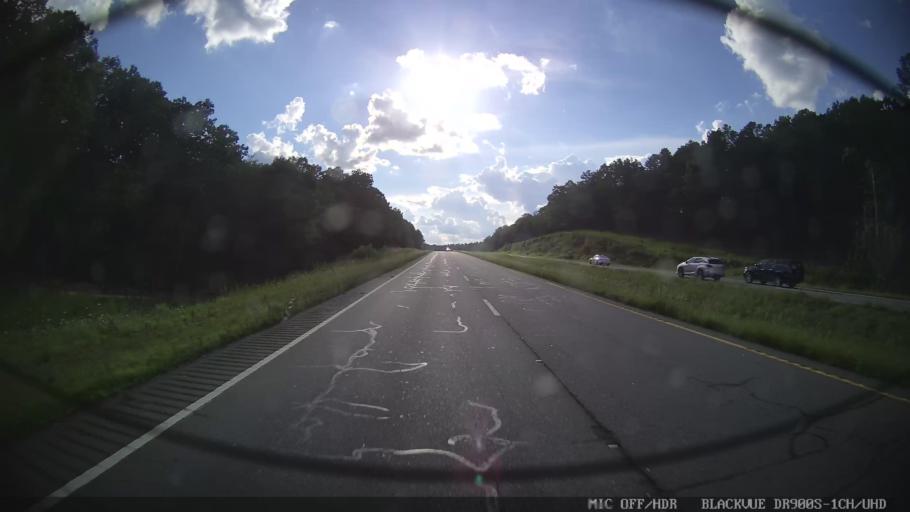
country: US
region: Georgia
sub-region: Bartow County
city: Euharlee
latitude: 34.2026
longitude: -85.0095
